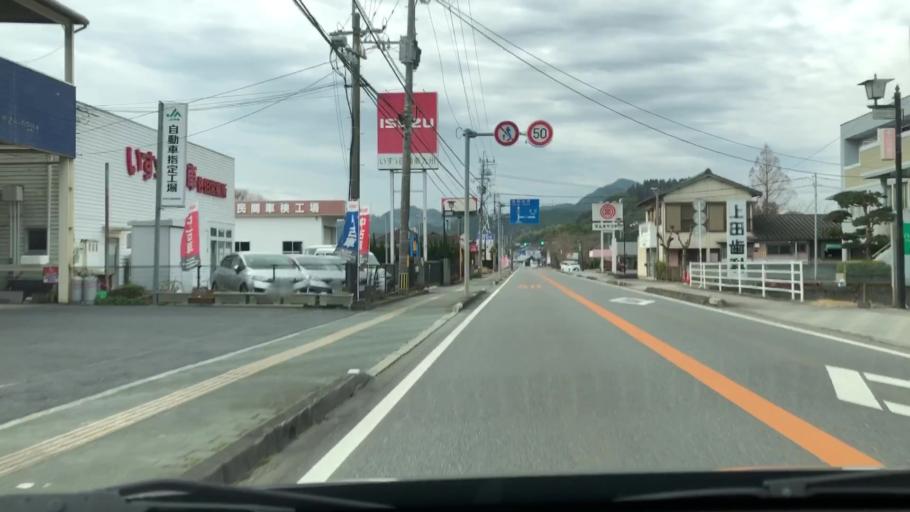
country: JP
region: Oita
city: Saiki
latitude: 32.9720
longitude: 131.8410
